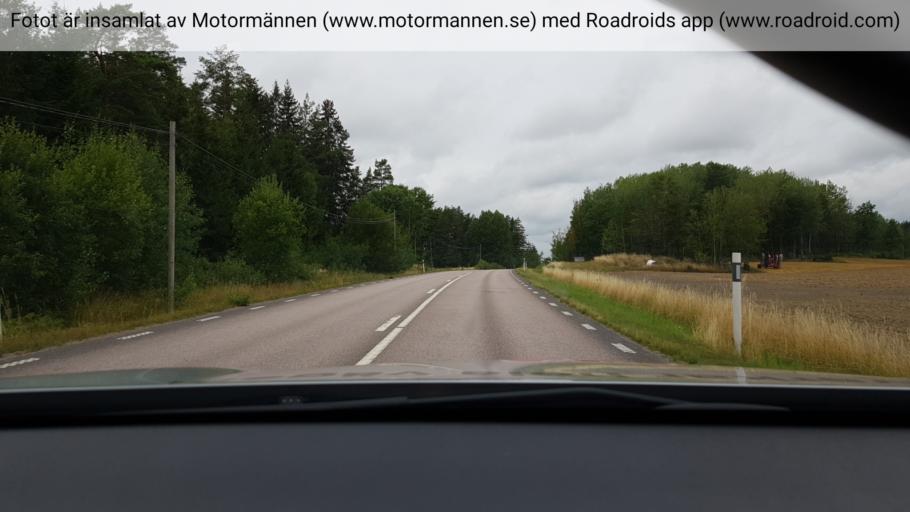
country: SE
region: Soedermanland
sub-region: Gnesta Kommun
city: Gnesta
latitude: 59.0545
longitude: 17.2028
